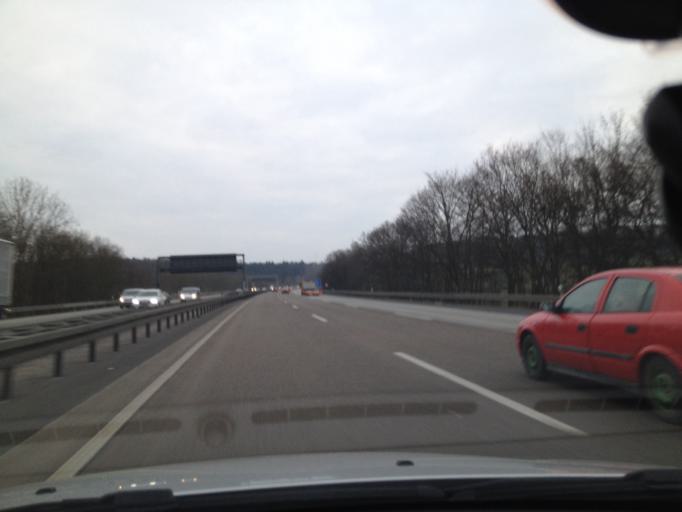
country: DE
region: Hesse
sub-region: Regierungsbezirk Giessen
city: Langgons
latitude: 50.4805
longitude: 8.7041
